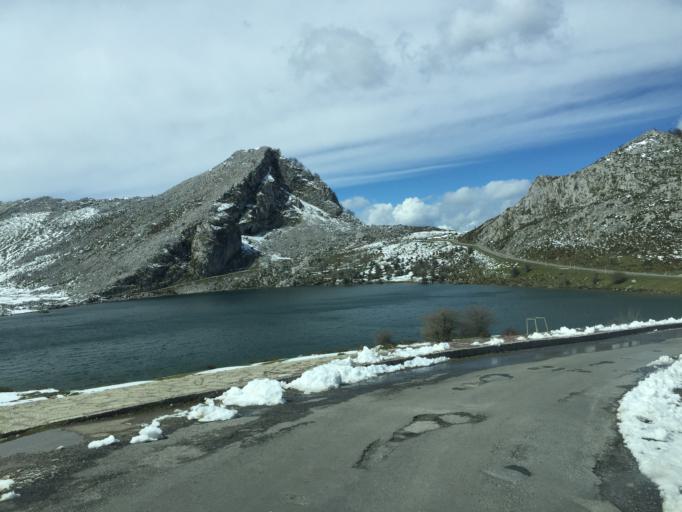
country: ES
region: Asturias
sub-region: Province of Asturias
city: Amieva
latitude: 43.2719
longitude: -4.9874
